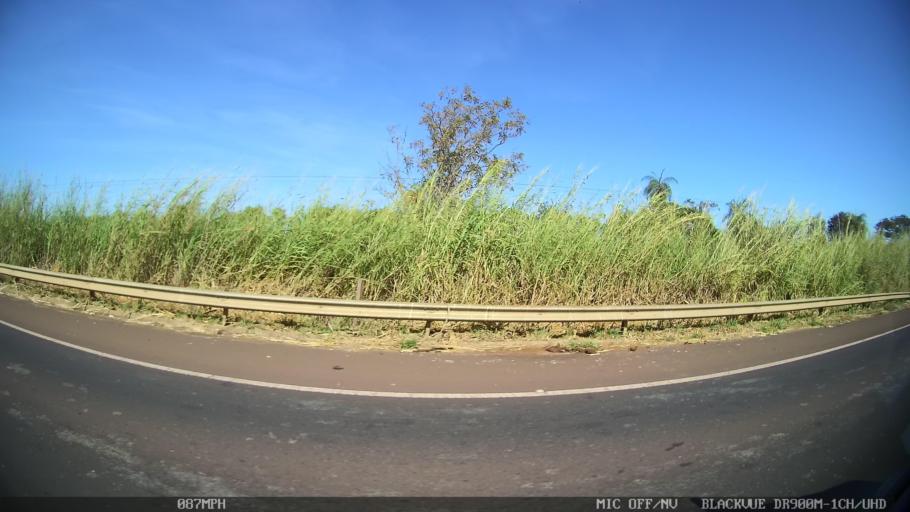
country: BR
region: Sao Paulo
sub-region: Barretos
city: Barretos
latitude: -20.5896
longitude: -48.7058
